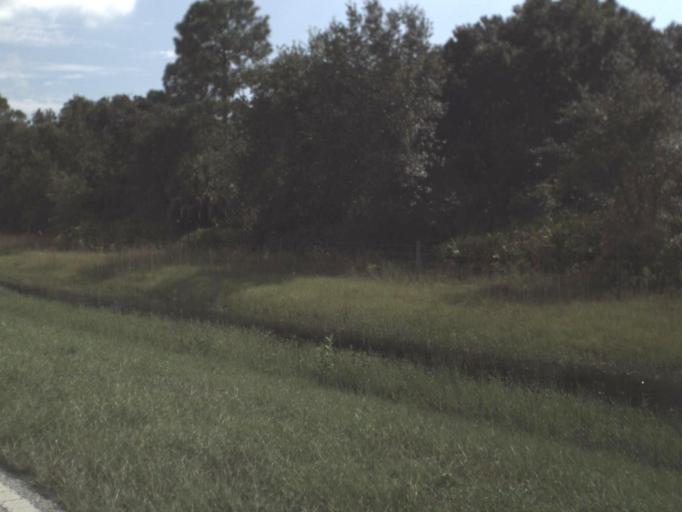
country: US
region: Florida
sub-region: Sarasota County
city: Plantation
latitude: 27.0835
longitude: -82.3334
